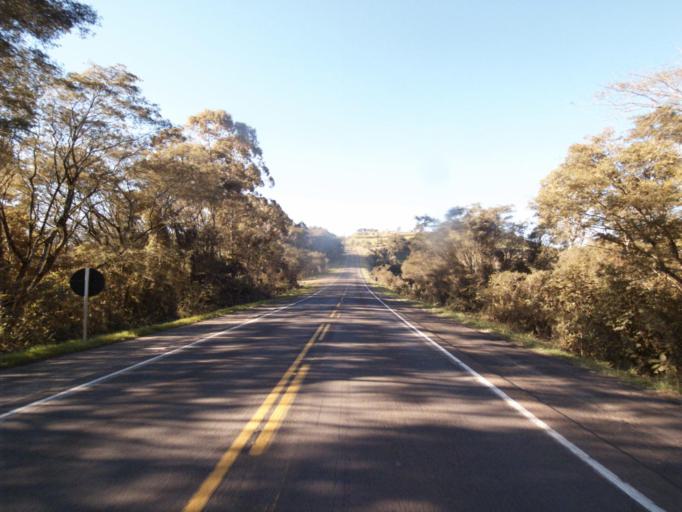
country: AR
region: Misiones
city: Bernardo de Irigoyen
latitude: -26.5037
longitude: -53.5101
